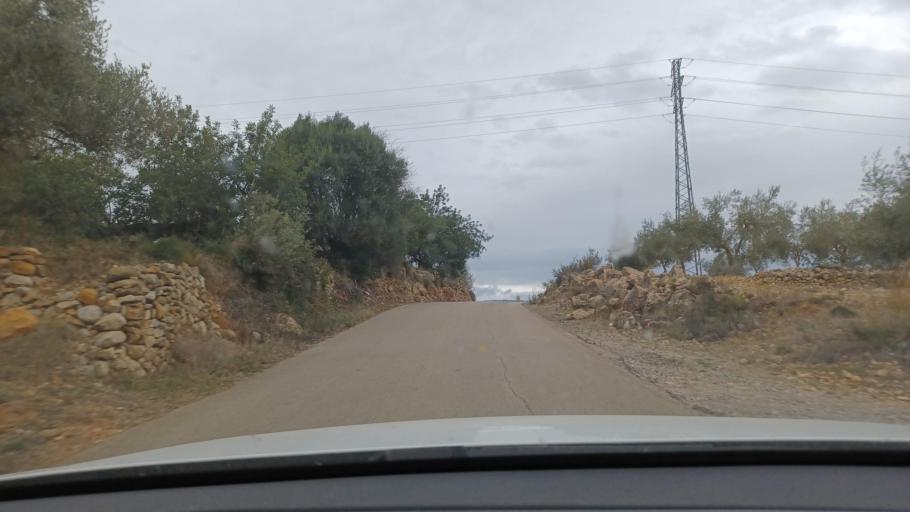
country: ES
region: Valencia
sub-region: Provincia de Castello
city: Traiguera
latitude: 40.5142
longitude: 0.2923
